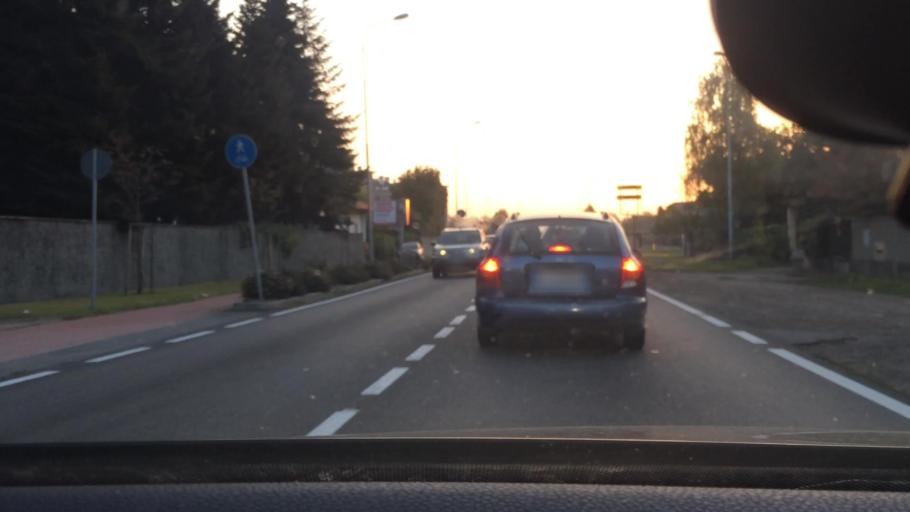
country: IT
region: Lombardy
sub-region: Citta metropolitana di Milano
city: Parabiago
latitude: 45.5470
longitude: 8.9426
